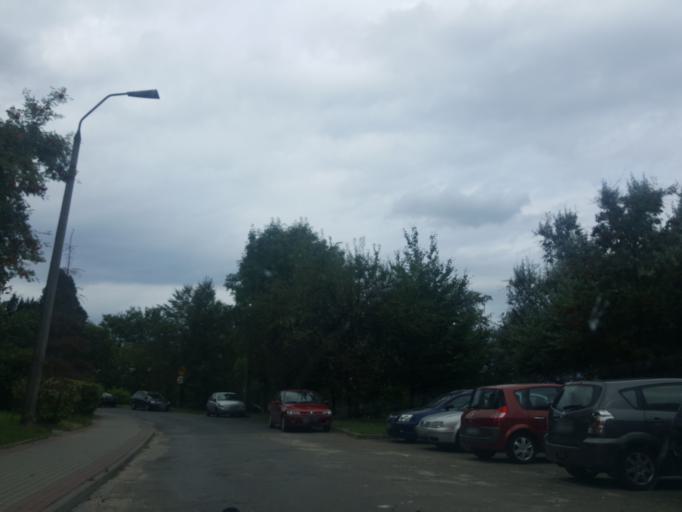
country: PL
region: Lesser Poland Voivodeship
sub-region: Powiat chrzanowski
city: Chrzanow
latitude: 50.1332
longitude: 19.4114
